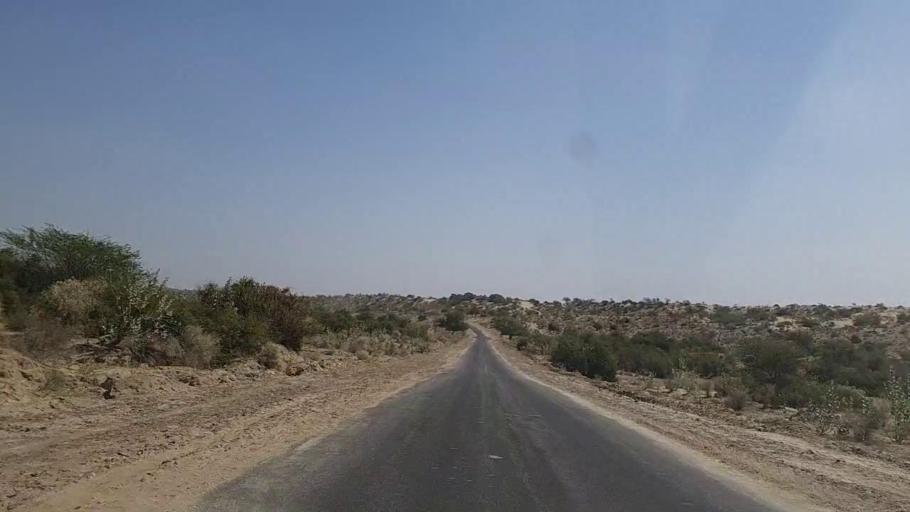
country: PK
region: Sindh
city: Diplo
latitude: 24.4817
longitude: 69.4818
